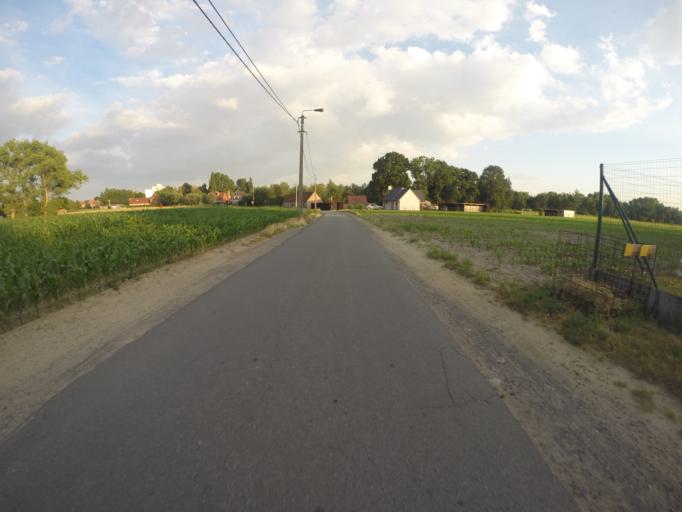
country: BE
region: Flanders
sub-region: Provincie West-Vlaanderen
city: Beernem
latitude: 51.1422
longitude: 3.3278
